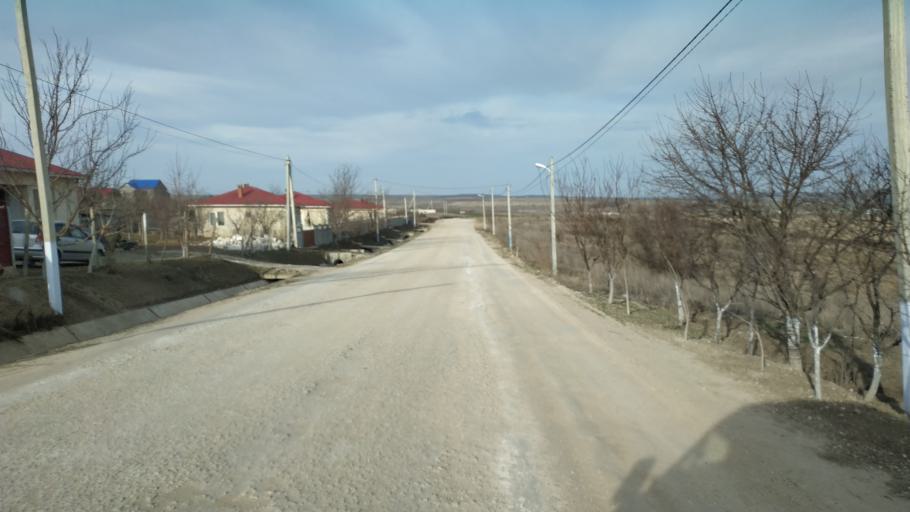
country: RO
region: Vaslui
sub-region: Comuna Dranceni
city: Dranceni
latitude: 46.8446
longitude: 28.1894
